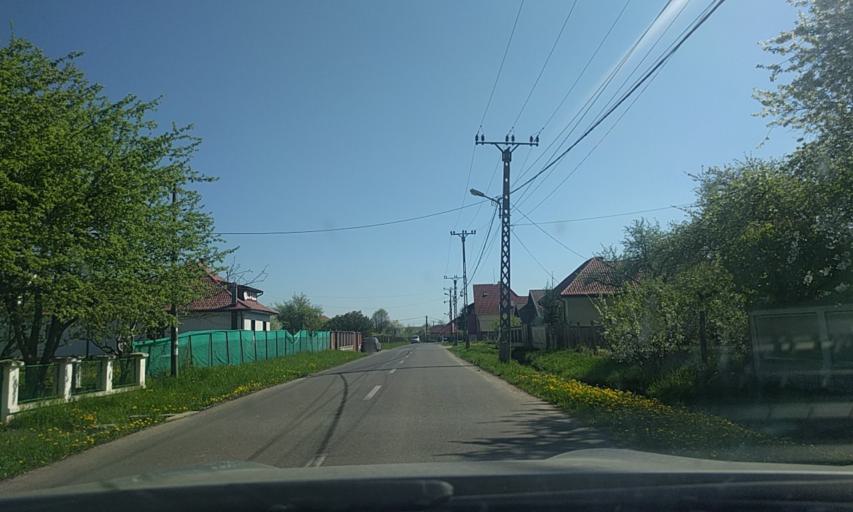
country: RO
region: Brasov
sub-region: Comuna Bod
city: Colonia Bod
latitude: 45.7139
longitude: 25.5738
